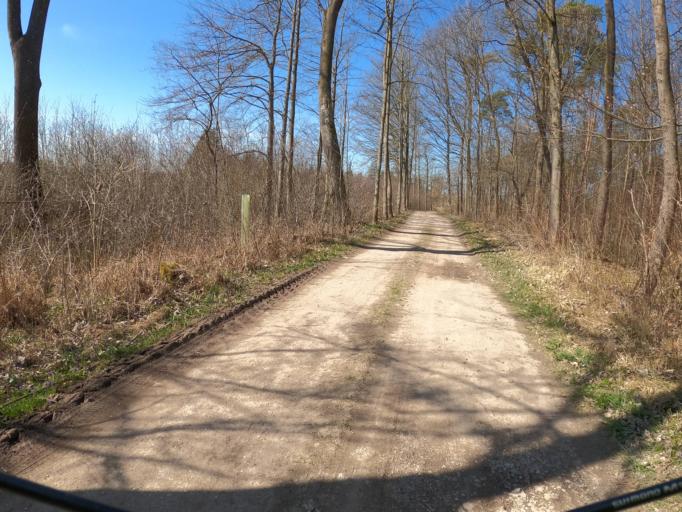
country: DE
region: Bavaria
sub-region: Swabia
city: Nersingen
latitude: 48.4364
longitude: 10.1421
